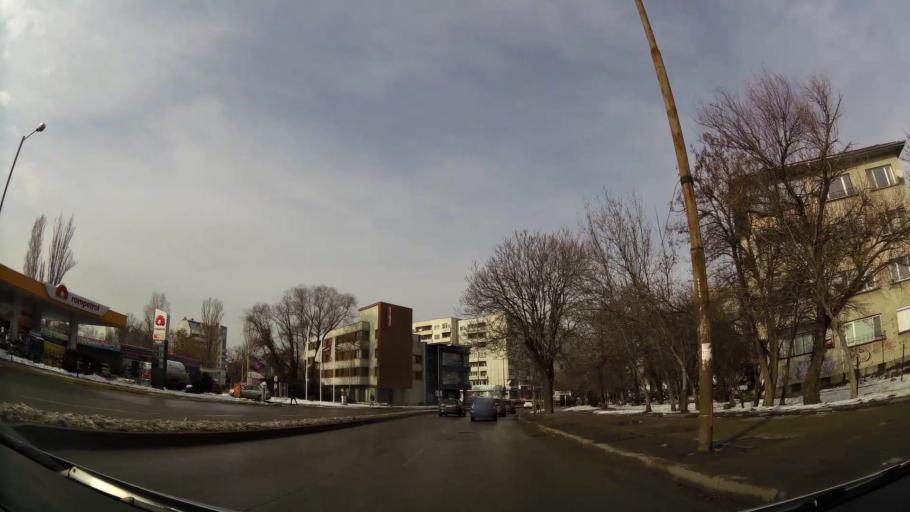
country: BG
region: Sofia-Capital
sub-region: Stolichna Obshtina
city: Sofia
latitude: 42.6993
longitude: 23.3609
